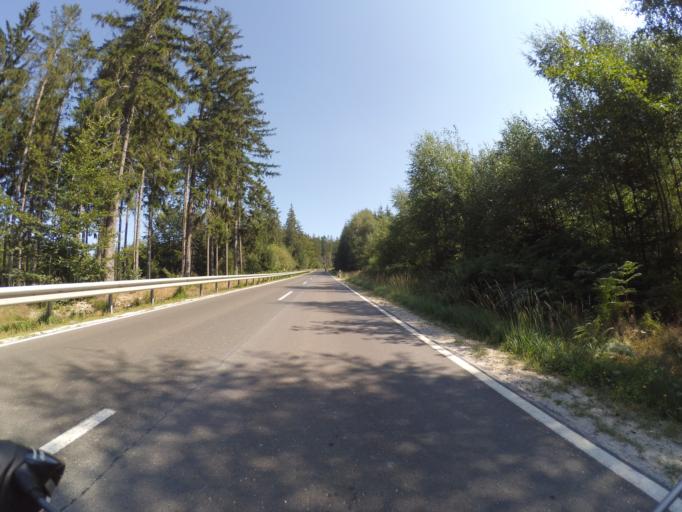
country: DE
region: Rheinland-Pfalz
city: Morbach
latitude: 49.7697
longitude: 7.1107
